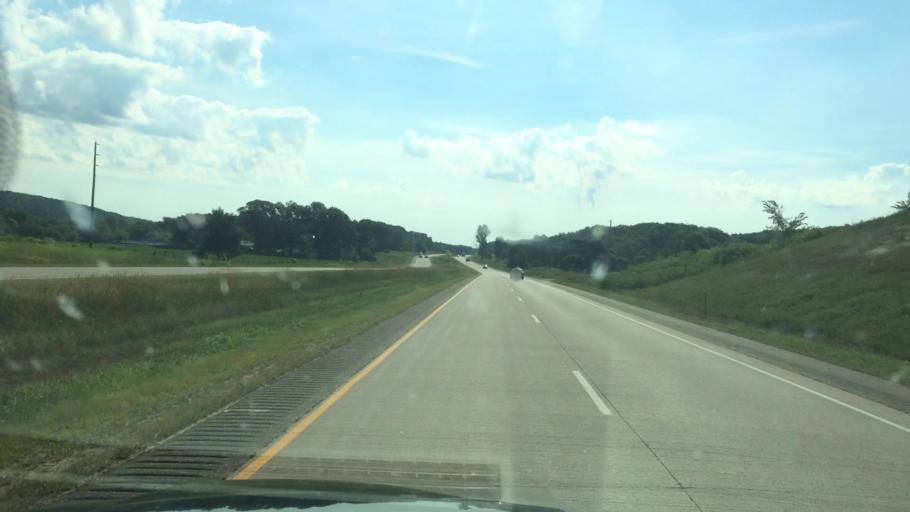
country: US
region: Wisconsin
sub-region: Shawano County
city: Wittenberg
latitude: 44.8258
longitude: -89.0922
